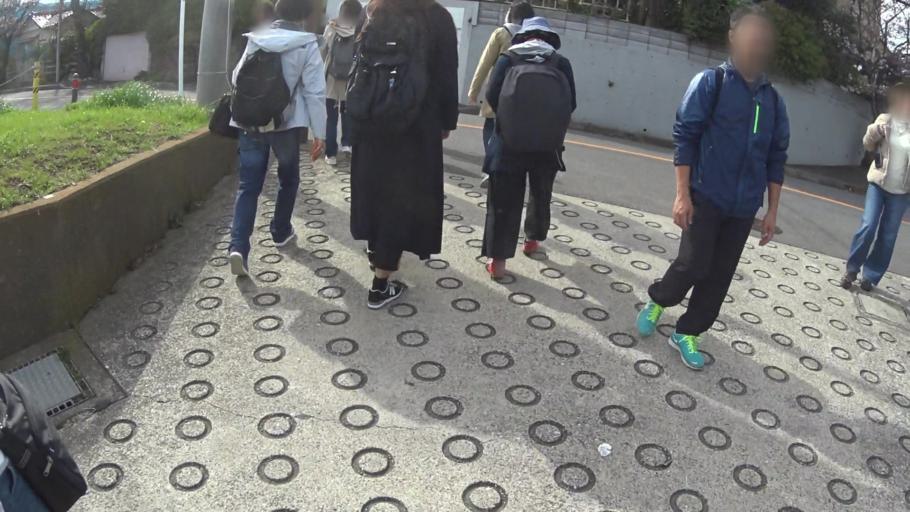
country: JP
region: Kanagawa
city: Kamakura
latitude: 35.3239
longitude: 139.5138
